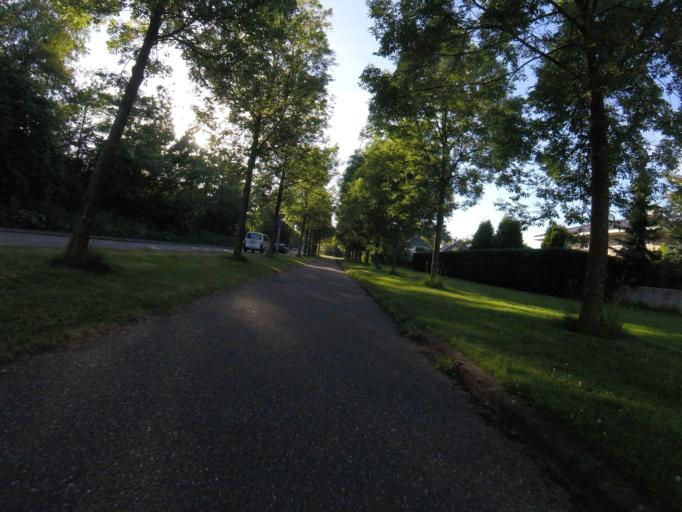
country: NL
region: North Holland
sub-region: Gemeente Haarlemmermeer
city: Hoofddorp
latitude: 52.3186
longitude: 4.6741
